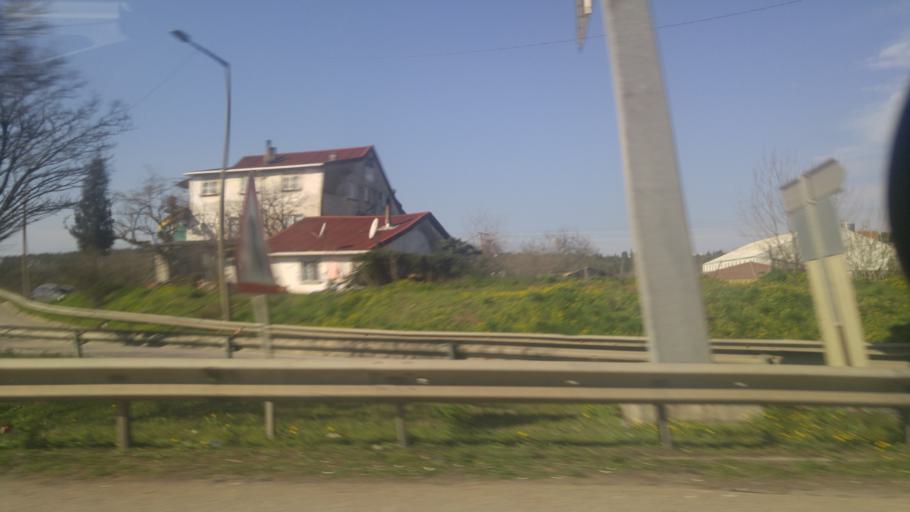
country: TR
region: Kocaeli
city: Darica
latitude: 40.8186
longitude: 29.3648
